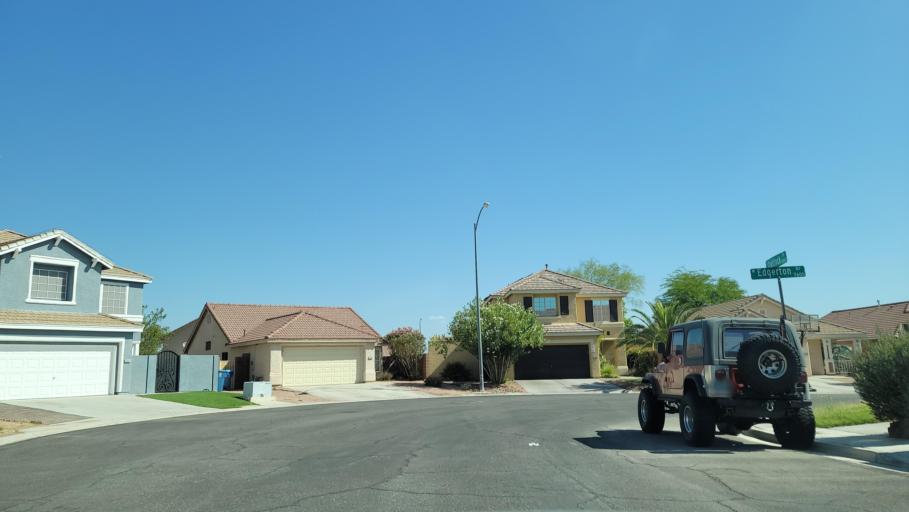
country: US
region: Nevada
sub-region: Clark County
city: Spring Valley
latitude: 36.0876
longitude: -115.2571
